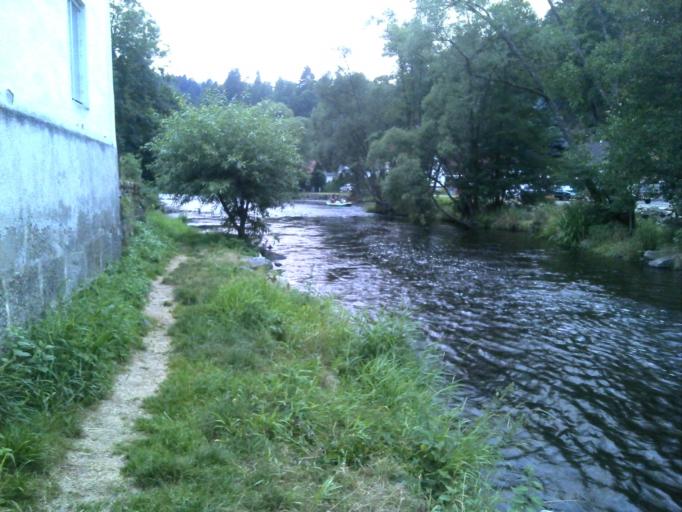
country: CZ
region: Jihocesky
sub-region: Okres Cesky Krumlov
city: Vyssi Brod
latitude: 48.6547
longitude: 14.3648
